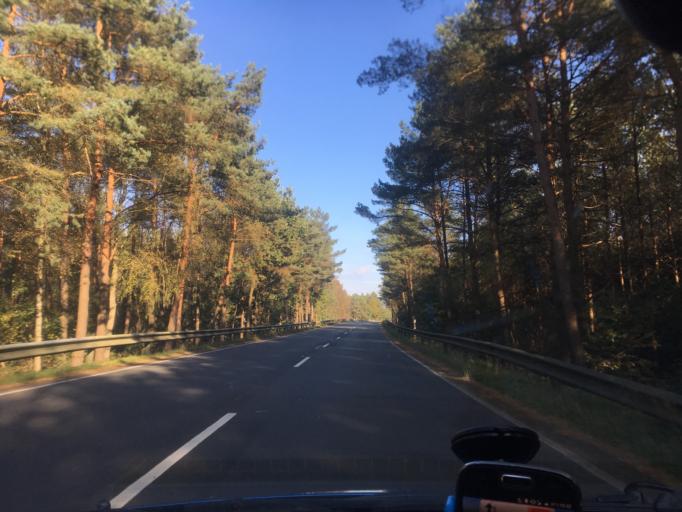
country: DE
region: Lower Saxony
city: Wietzendorf
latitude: 52.9306
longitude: 9.9345
